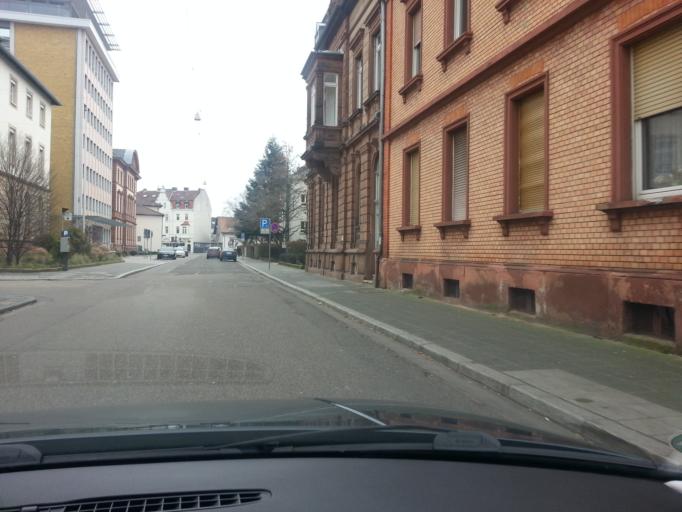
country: DE
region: Rheinland-Pfalz
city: Frankenthal
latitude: 49.5389
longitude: 8.3516
